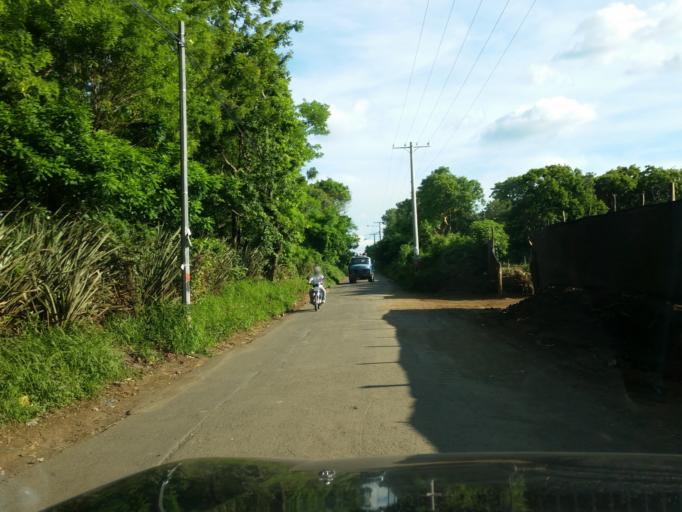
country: NI
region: Masaya
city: Ticuantepe
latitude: 12.0791
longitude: -86.2122
